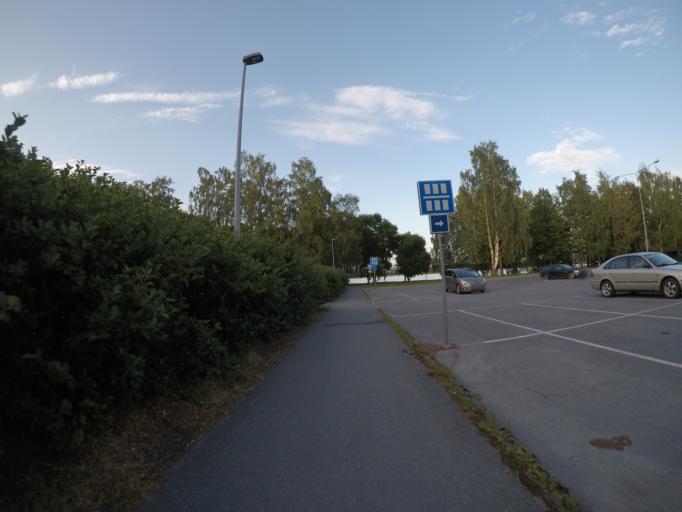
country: FI
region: Haeme
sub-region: Haemeenlinna
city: Haemeenlinna
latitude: 60.9932
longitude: 24.4657
